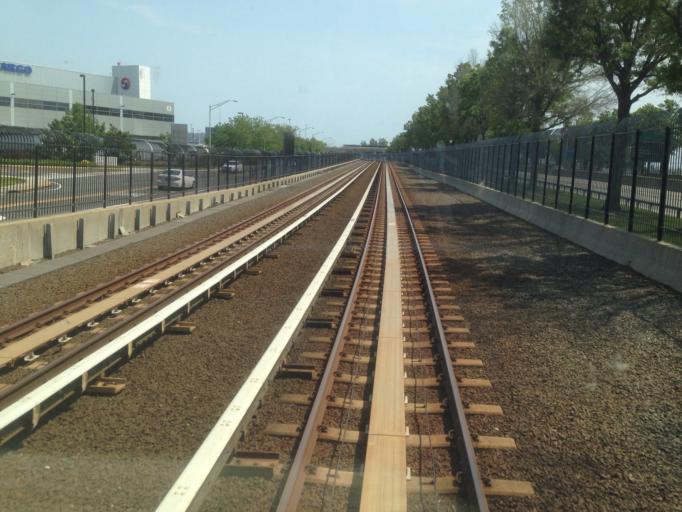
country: US
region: New York
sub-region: Queens County
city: Jamaica
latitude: 40.6531
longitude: -73.8064
